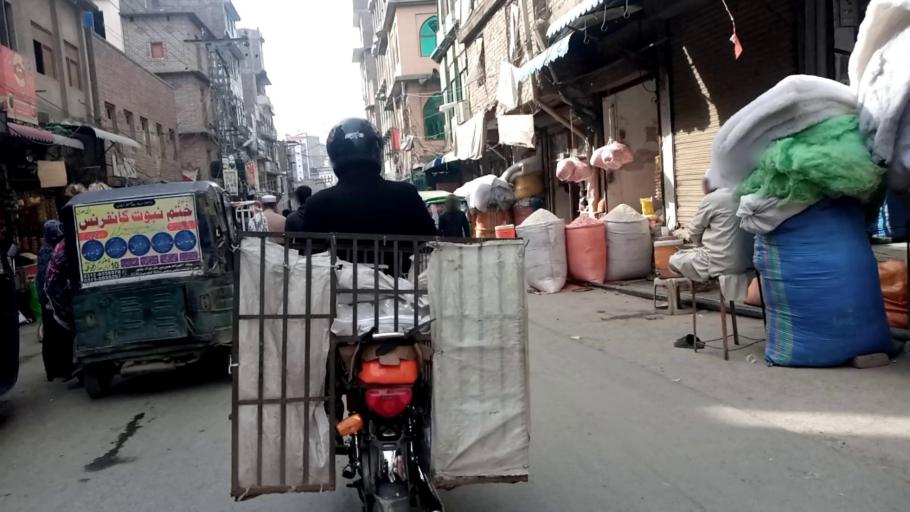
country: PK
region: Khyber Pakhtunkhwa
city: Peshawar
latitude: 34.0080
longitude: 71.5753
